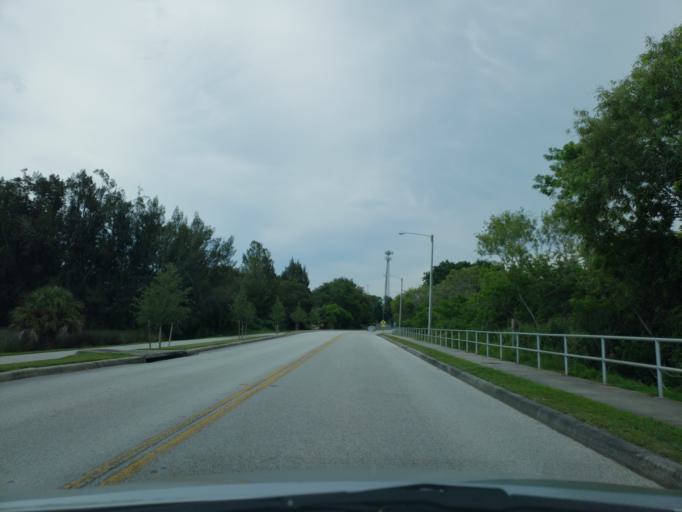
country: US
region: Florida
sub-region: Pinellas County
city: Tarpon Springs
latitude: 28.1541
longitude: -82.7510
